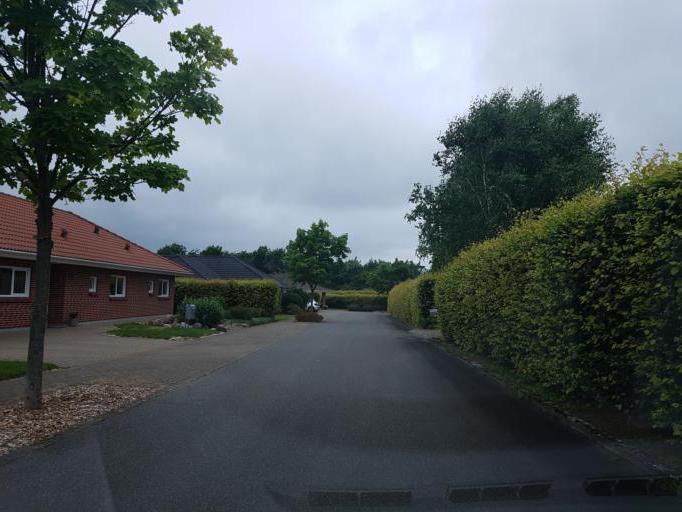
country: DK
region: South Denmark
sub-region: Varde Kommune
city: Varde
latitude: 55.6369
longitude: 8.4791
